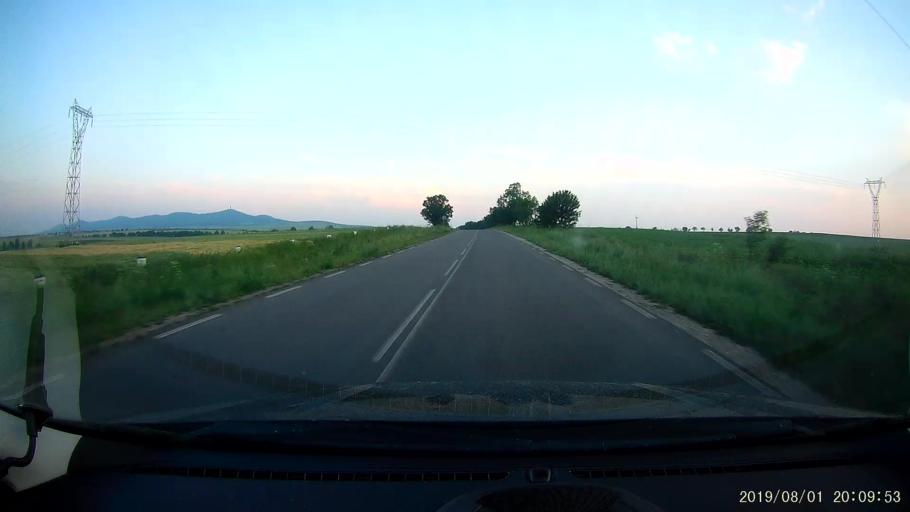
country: BG
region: Yambol
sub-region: Obshtina Yambol
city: Yambol
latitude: 42.4910
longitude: 26.5948
